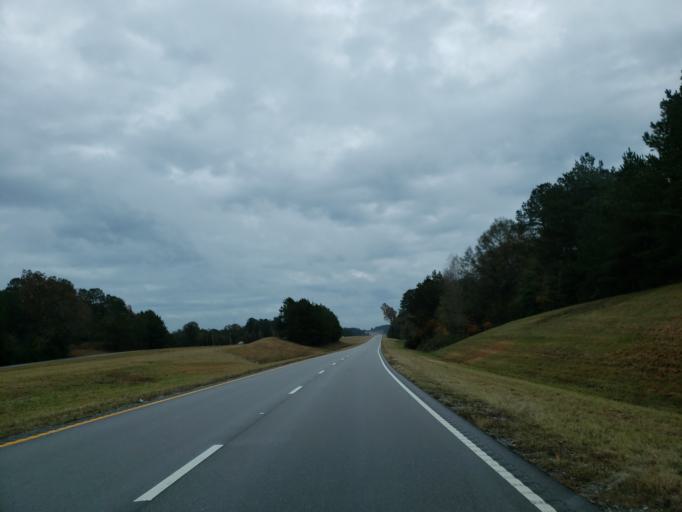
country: US
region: Mississippi
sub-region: Wayne County
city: Waynesboro
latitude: 31.6949
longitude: -88.7202
